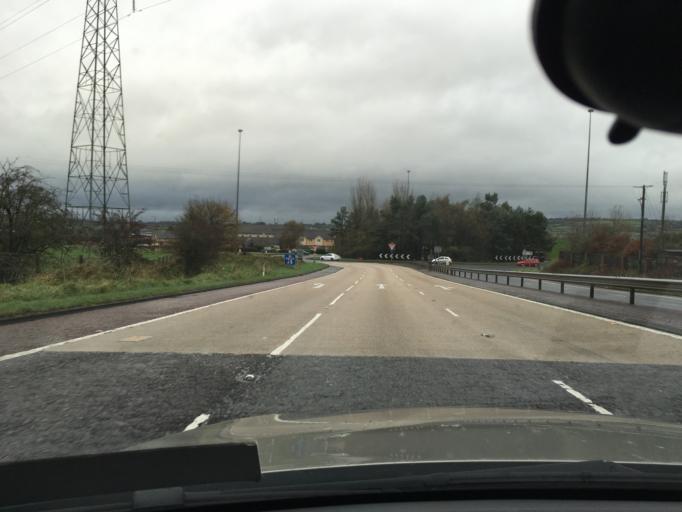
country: GB
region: Northern Ireland
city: Carnmoney
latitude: 54.6913
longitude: -5.9715
